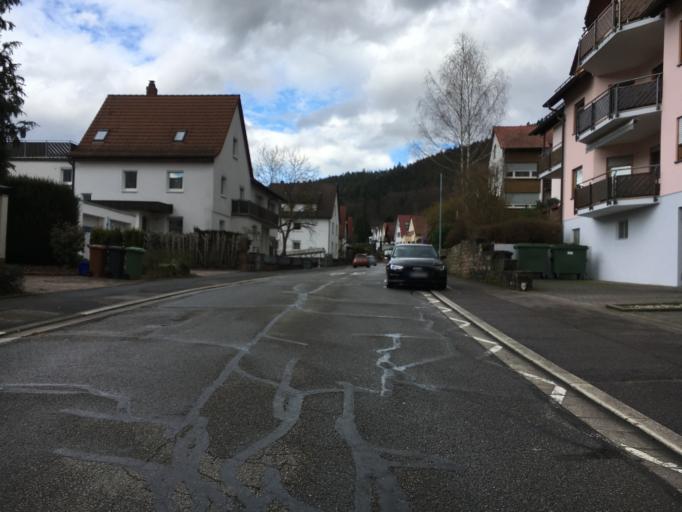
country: DE
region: Baden-Wuerttemberg
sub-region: Karlsruhe Region
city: Eberbach
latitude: 49.4672
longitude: 8.9928
